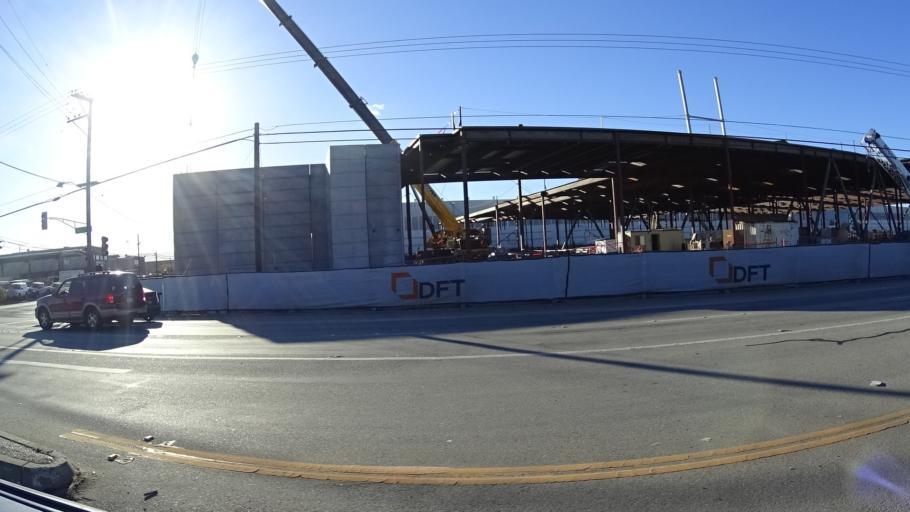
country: US
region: California
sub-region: Santa Clara County
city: Santa Clara
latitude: 37.3610
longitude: -121.9414
